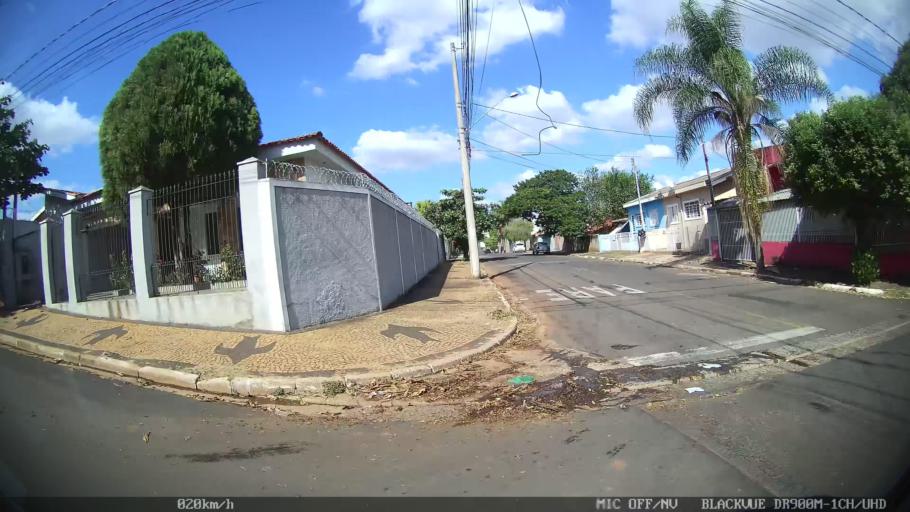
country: BR
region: Sao Paulo
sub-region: Sumare
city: Sumare
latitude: -22.8267
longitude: -47.2763
